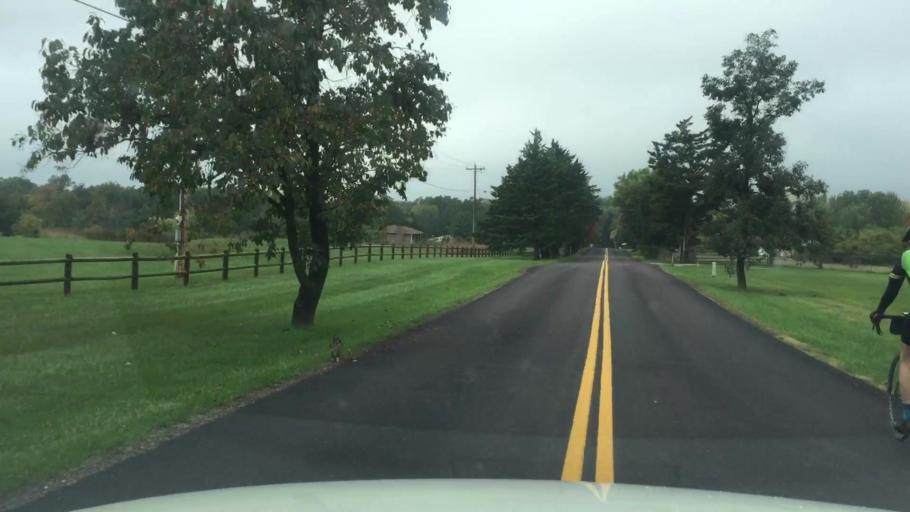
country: US
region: Missouri
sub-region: Boone County
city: Columbia
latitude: 38.8601
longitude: -92.3286
